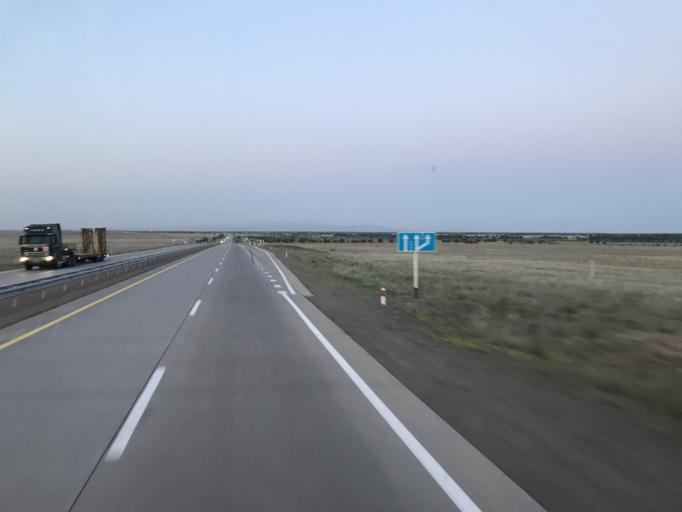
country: KZ
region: Almaty Oblysy
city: Kapshagay
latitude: 43.9716
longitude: 77.3751
